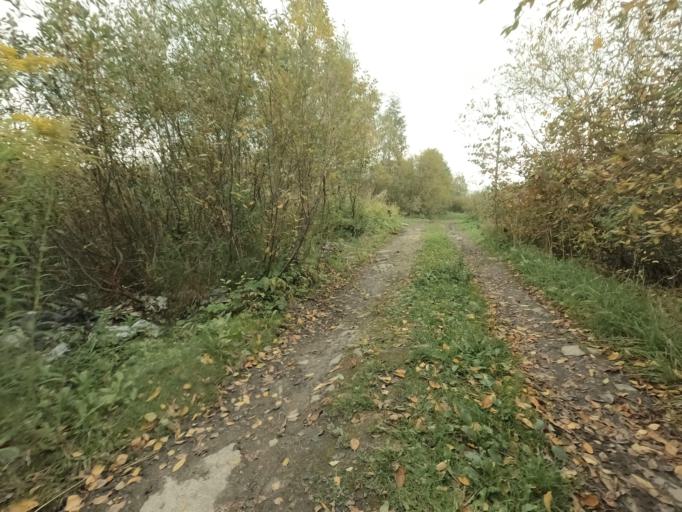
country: RU
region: St.-Petersburg
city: Sapernyy
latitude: 59.7780
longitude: 30.6400
